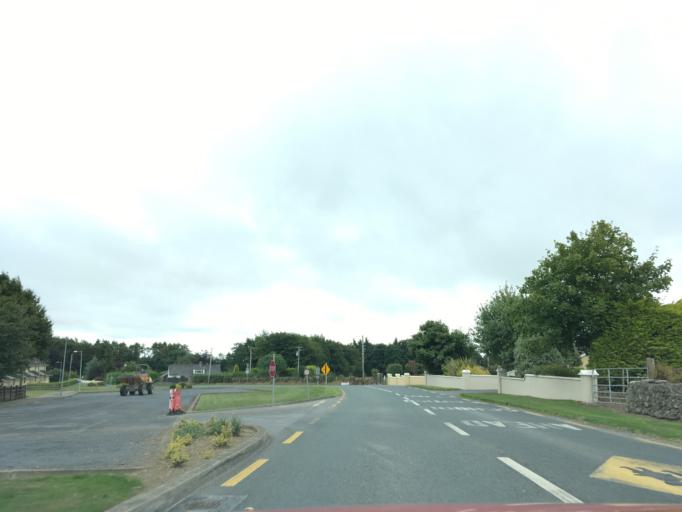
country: IE
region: Munster
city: Cashel
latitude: 52.4671
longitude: -7.8319
